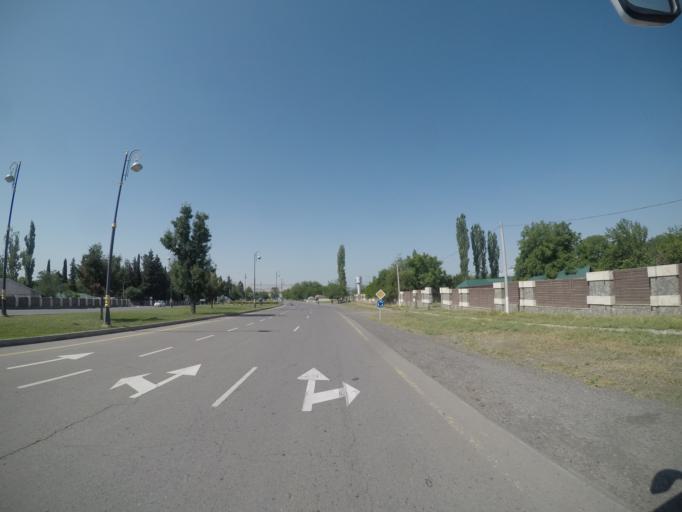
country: AZ
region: Qabala Rayon
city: Qutqashen
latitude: 40.8615
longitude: 47.7567
